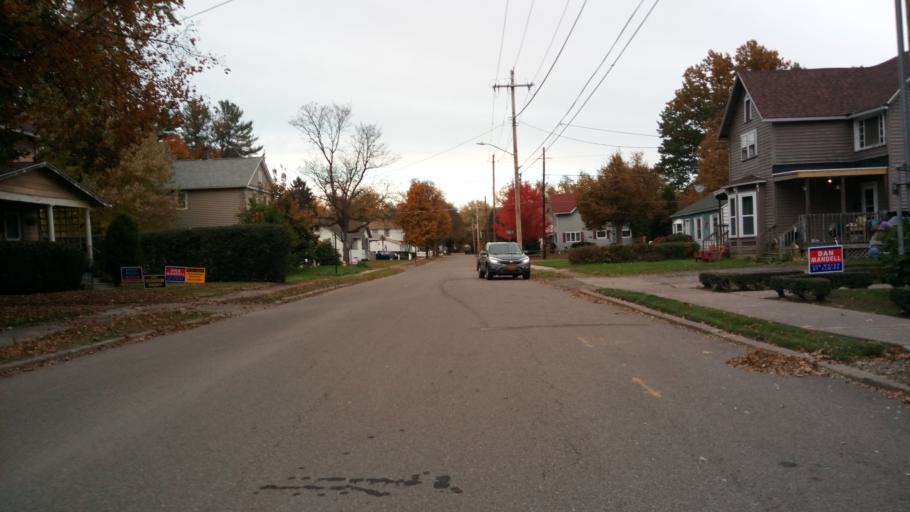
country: US
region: New York
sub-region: Chemung County
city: Elmira
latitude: 42.0789
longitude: -76.7959
